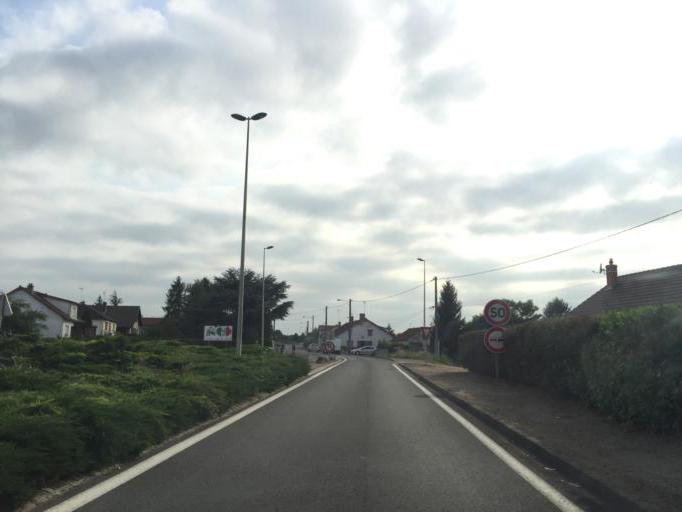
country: FR
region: Auvergne
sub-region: Departement de l'Allier
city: Molinet
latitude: 46.4693
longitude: 3.9417
